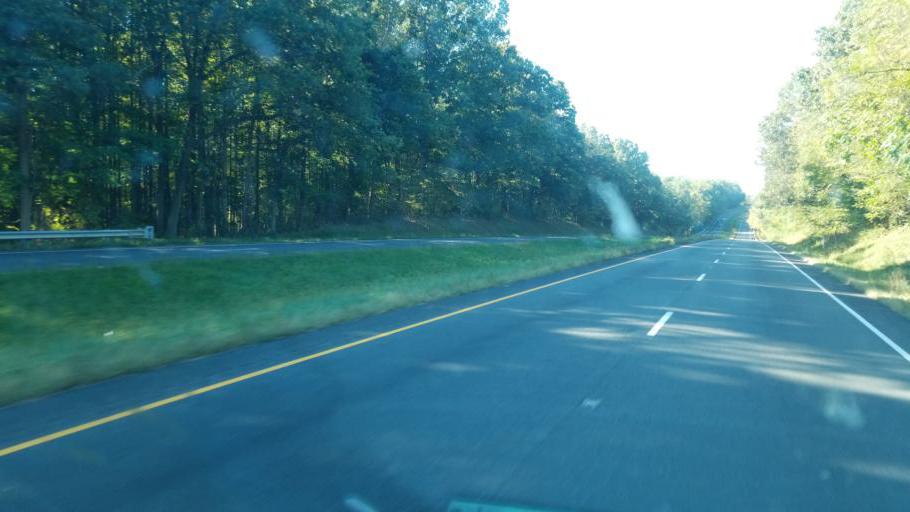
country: US
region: Virginia
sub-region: Madison County
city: Madison
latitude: 38.3884
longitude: -78.2445
